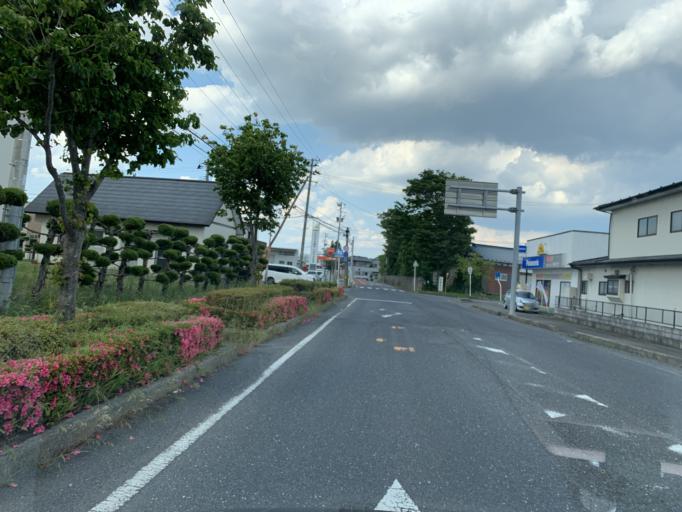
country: JP
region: Miyagi
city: Wakuya
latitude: 38.6284
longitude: 141.1905
